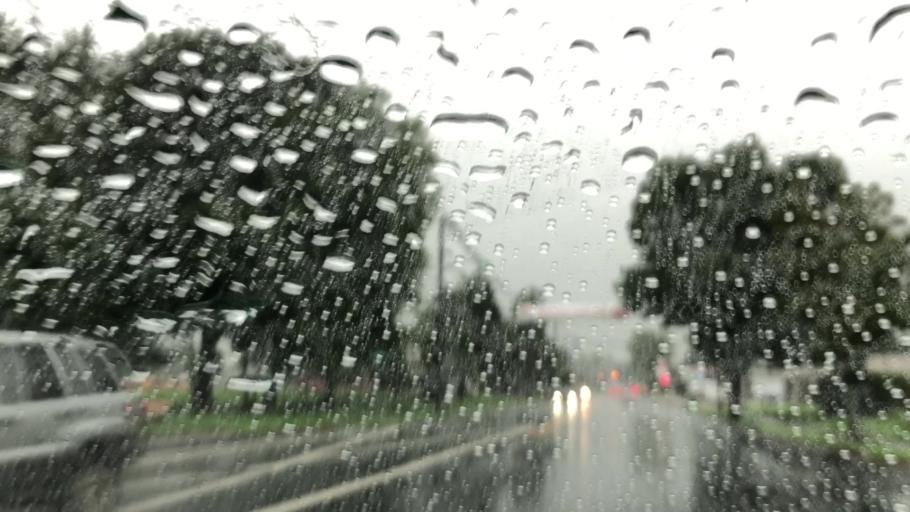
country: US
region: New Jersey
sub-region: Bergen County
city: Saddle Brook
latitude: 40.8964
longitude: -74.0910
